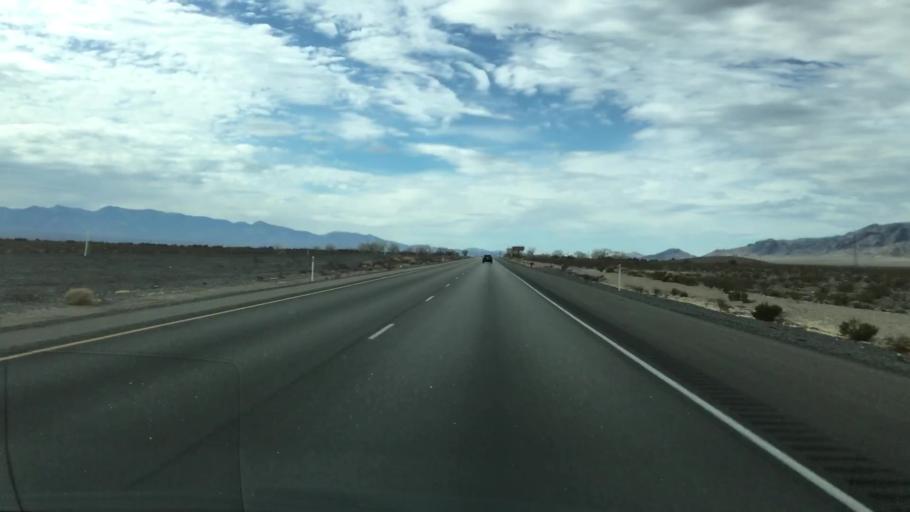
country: US
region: Nevada
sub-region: Nye County
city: Pahrump
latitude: 36.5800
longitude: -115.7120
